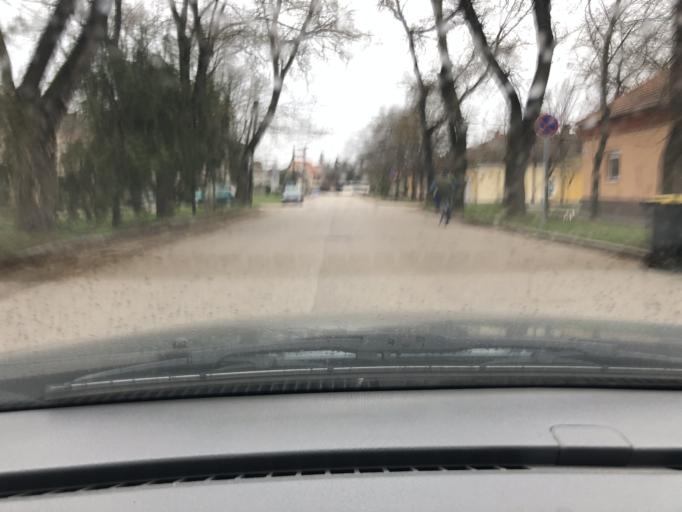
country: HU
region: Csongrad
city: Csongrad
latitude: 46.7056
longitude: 20.1463
